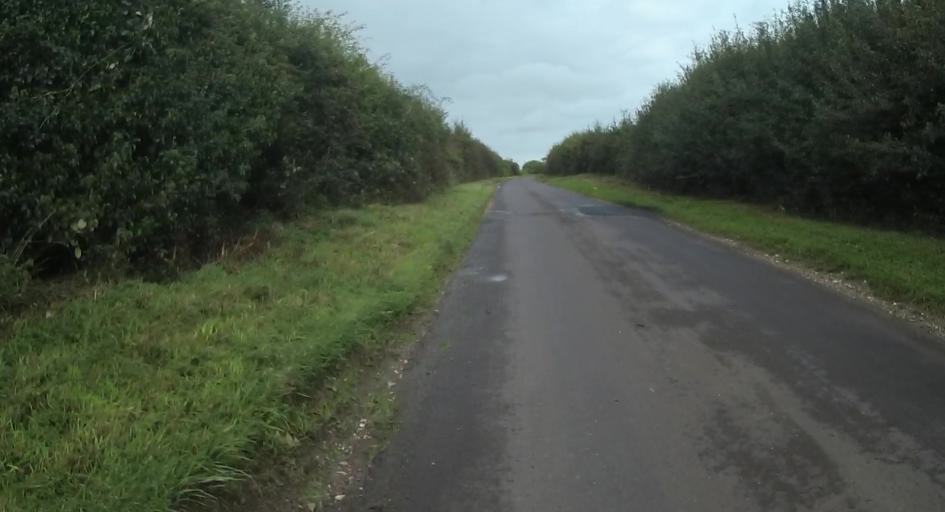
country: GB
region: England
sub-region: Hampshire
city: Basingstoke
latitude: 51.2820
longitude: -1.1441
